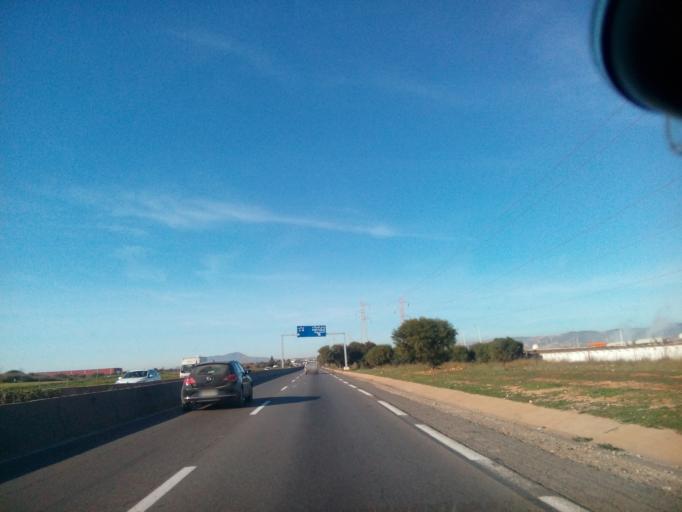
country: DZ
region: Oran
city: Ain el Bya
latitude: 35.8002
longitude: -0.3315
